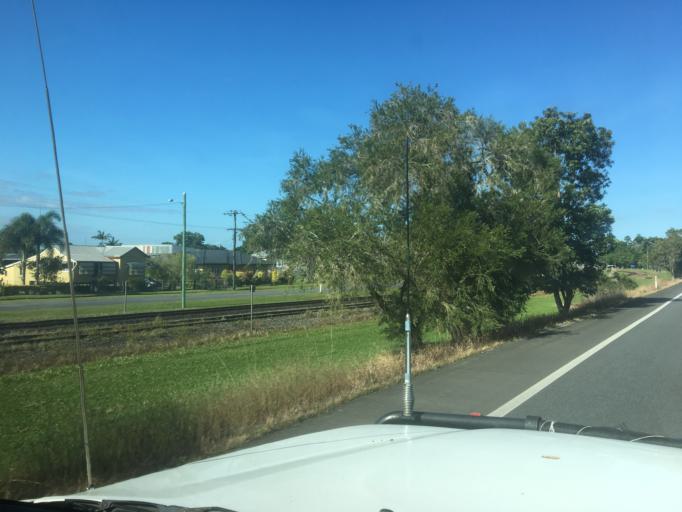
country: AU
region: Queensland
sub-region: Cassowary Coast
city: Innisfail
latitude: -17.3384
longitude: 145.9267
